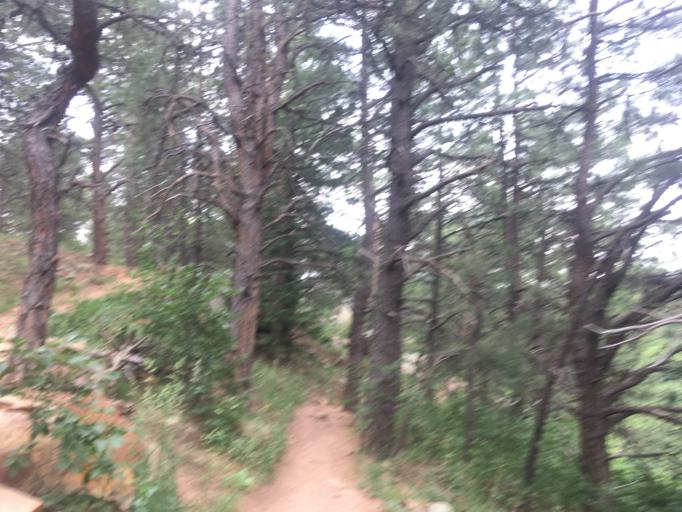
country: US
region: Colorado
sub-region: Boulder County
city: Boulder
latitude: 39.9526
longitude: -105.2777
